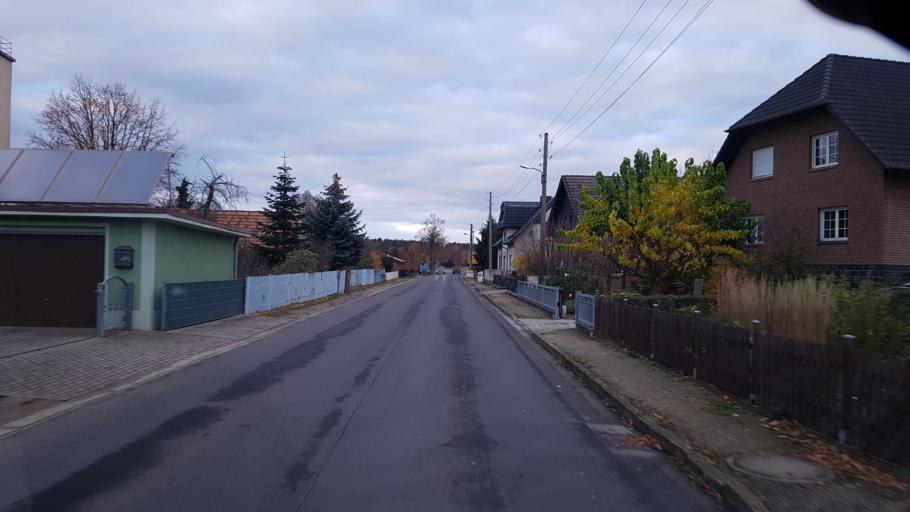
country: DE
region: Brandenburg
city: Ortrand
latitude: 51.3812
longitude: 13.7590
